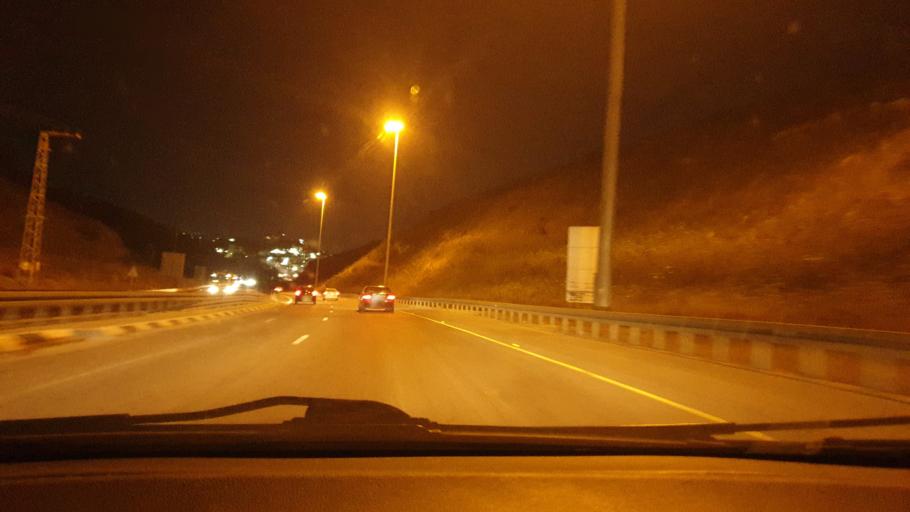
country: IL
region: Haifa
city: Umm el Fahm
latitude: 32.5504
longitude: 35.1637
